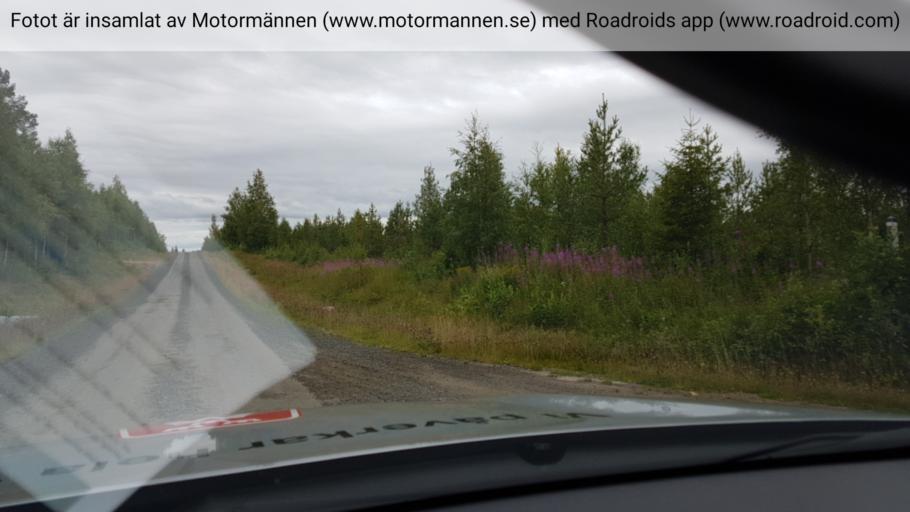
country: SE
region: Norrbotten
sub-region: Pajala Kommun
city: Pajala
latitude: 67.0409
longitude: 22.8428
